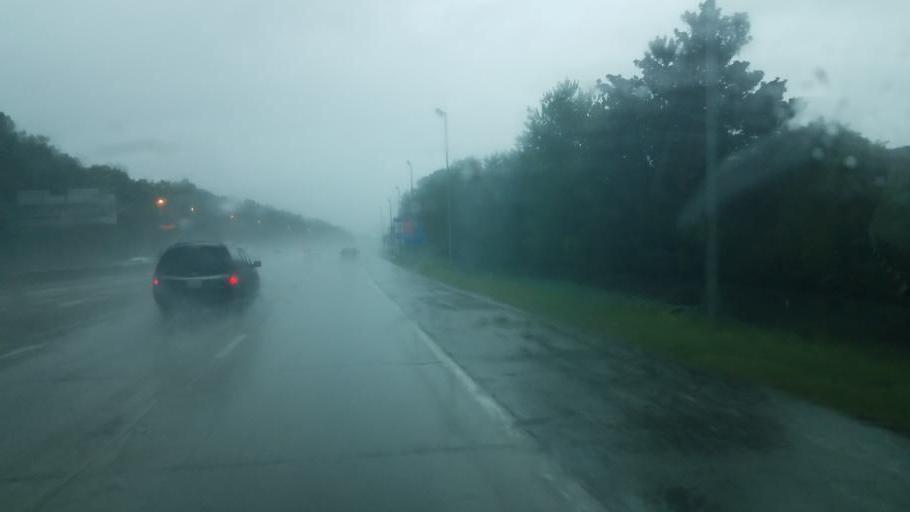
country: US
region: Virginia
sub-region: City of Poquoson
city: Poquoson
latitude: 37.0954
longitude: -76.4645
